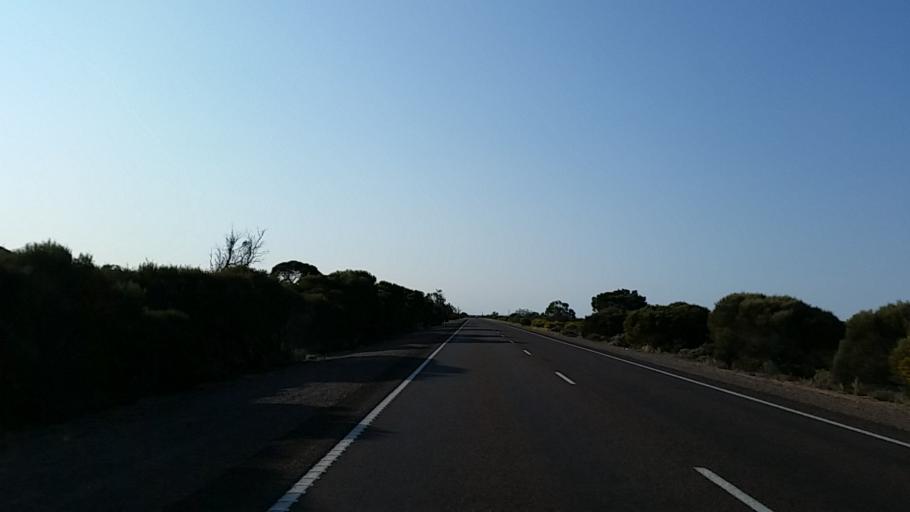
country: AU
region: South Australia
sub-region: Whyalla
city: Whyalla
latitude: -32.7560
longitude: 137.5254
